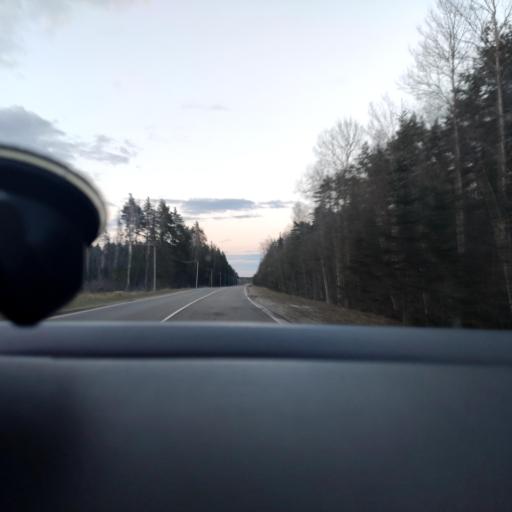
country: RU
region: Moskovskaya
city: Shaturtorf
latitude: 55.4498
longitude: 39.4389
